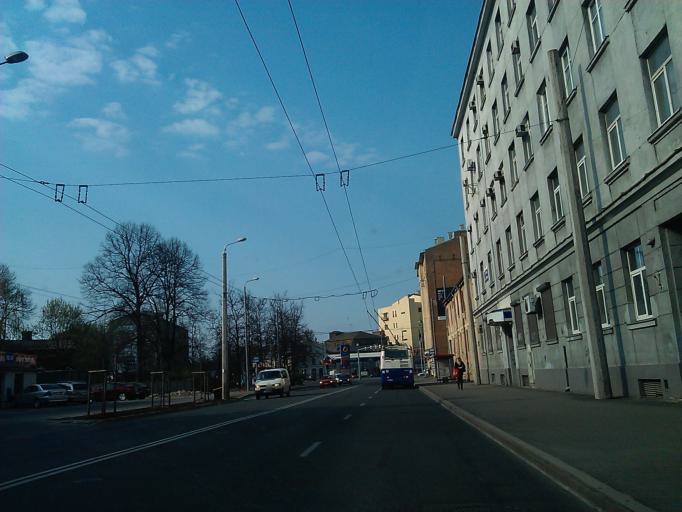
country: LV
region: Riga
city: Riga
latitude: 56.9626
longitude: 24.1512
